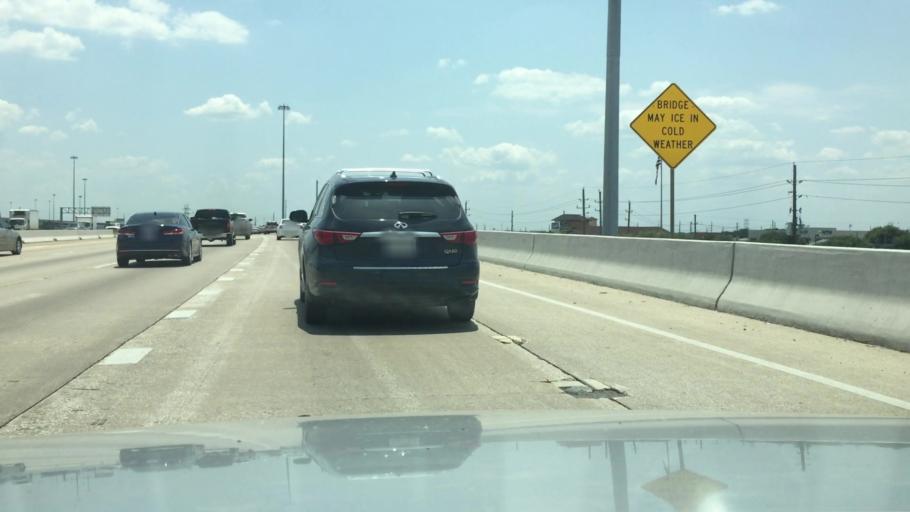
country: US
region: Texas
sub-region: Fort Bend County
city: Meadows Place
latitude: 29.6758
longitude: -95.5604
